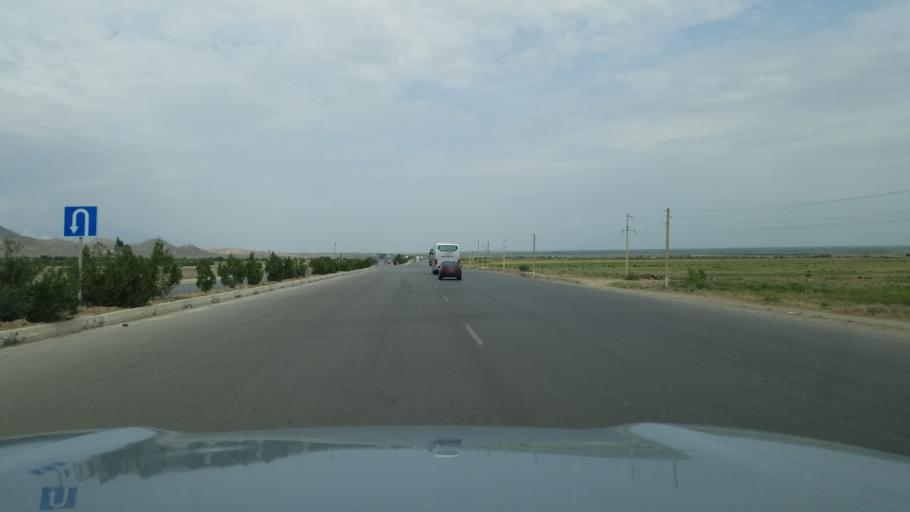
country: TM
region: Ahal
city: Baharly
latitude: 38.2357
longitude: 57.7765
